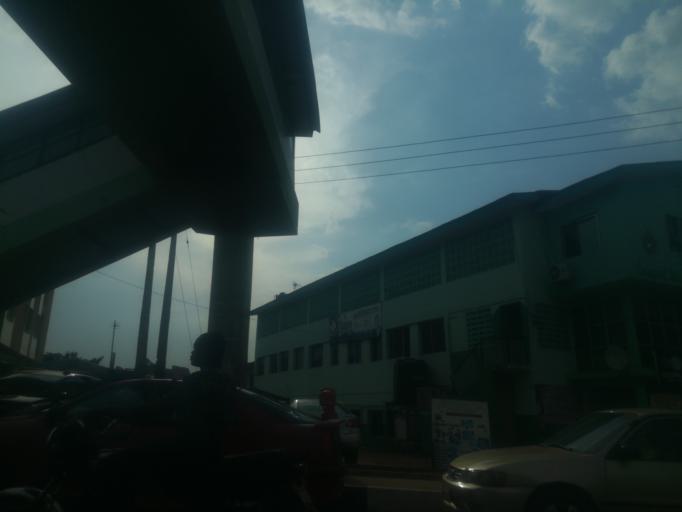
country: NG
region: Ogun
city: Abeokuta
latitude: 7.1443
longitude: 3.3307
